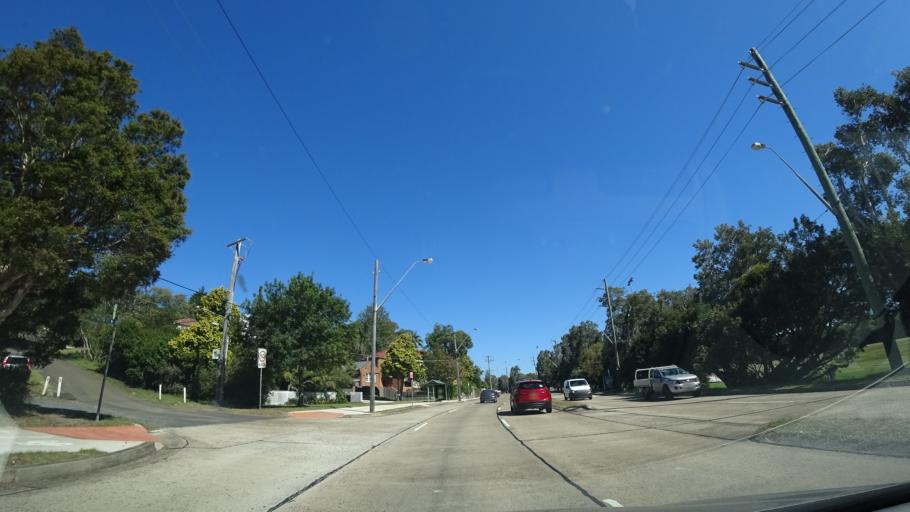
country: AU
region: New South Wales
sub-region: Warringah
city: North Manly
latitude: -33.7773
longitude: 151.2740
